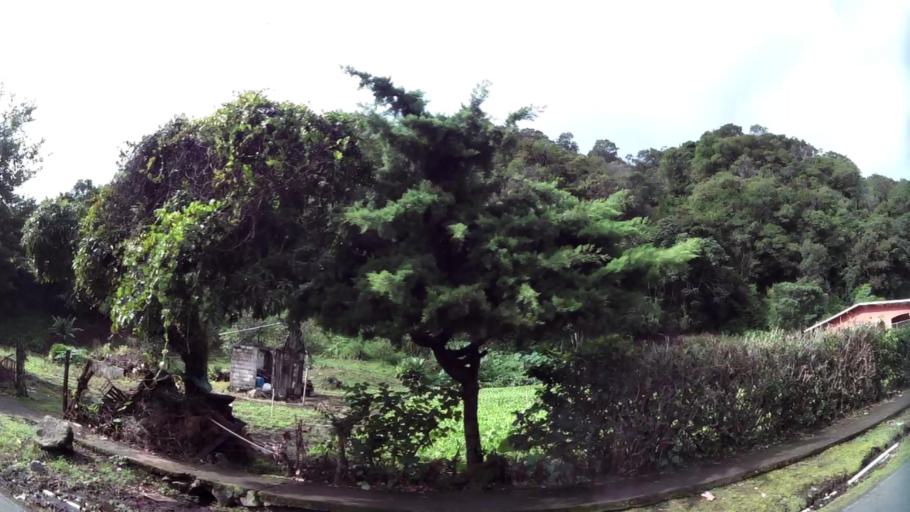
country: PA
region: Chiriqui
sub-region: Distrito Boquete
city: Boquete
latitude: 8.7974
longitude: -82.4500
